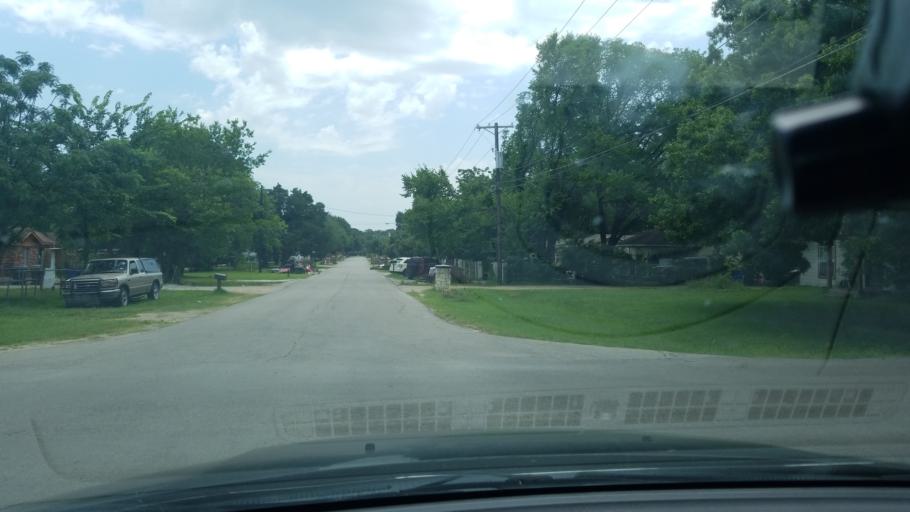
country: US
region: Texas
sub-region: Dallas County
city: Balch Springs
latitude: 32.7226
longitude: -96.6585
